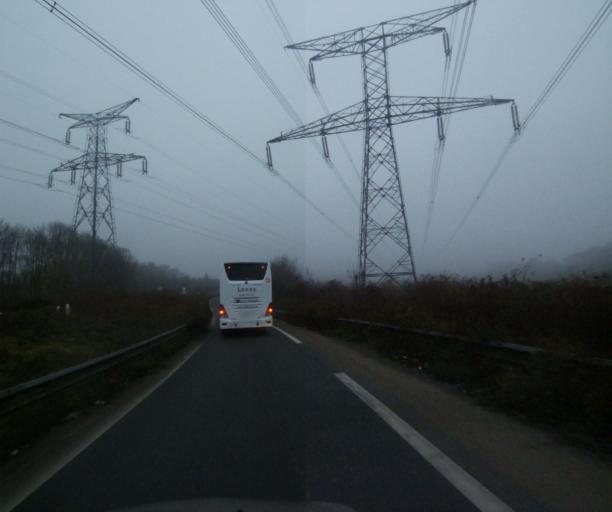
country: FR
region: Ile-de-France
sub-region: Departement de Seine-et-Marne
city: Saint-Thibault-des-Vignes
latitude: 48.8606
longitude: 2.6652
